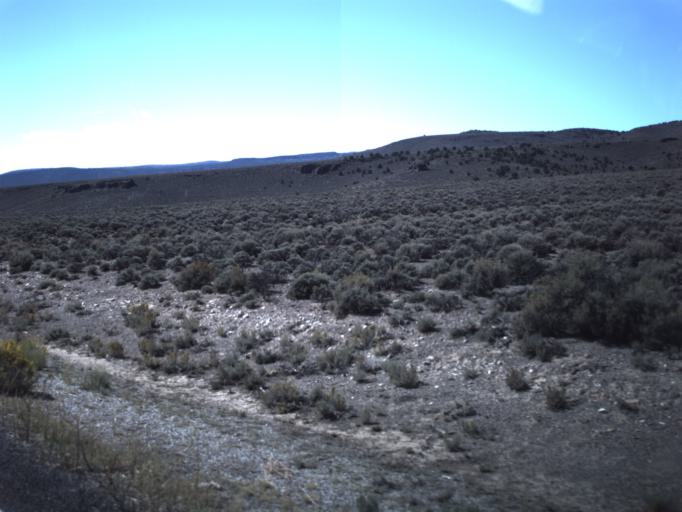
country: US
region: Utah
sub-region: Piute County
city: Junction
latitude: 38.1950
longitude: -112.0105
